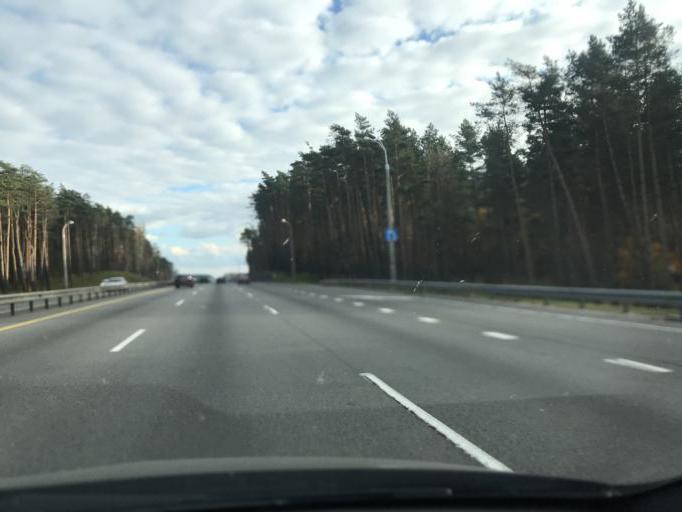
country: BY
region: Minsk
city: Bal'shavik
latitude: 53.9681
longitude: 27.6034
